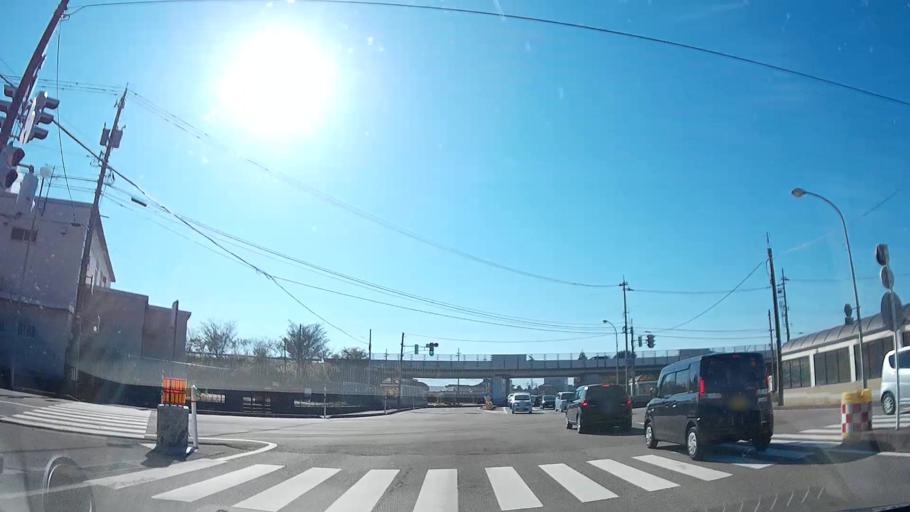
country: JP
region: Toyama
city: Nanto-shi
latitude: 36.6236
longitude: 136.9429
